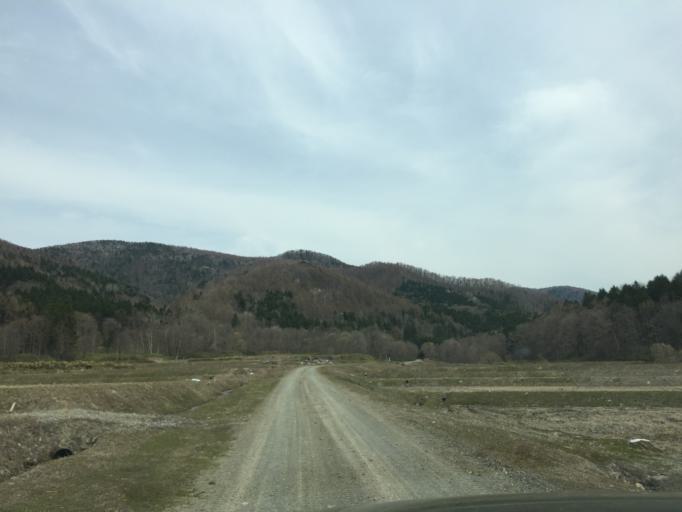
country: JP
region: Hokkaido
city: Ashibetsu
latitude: 43.6221
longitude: 142.2243
